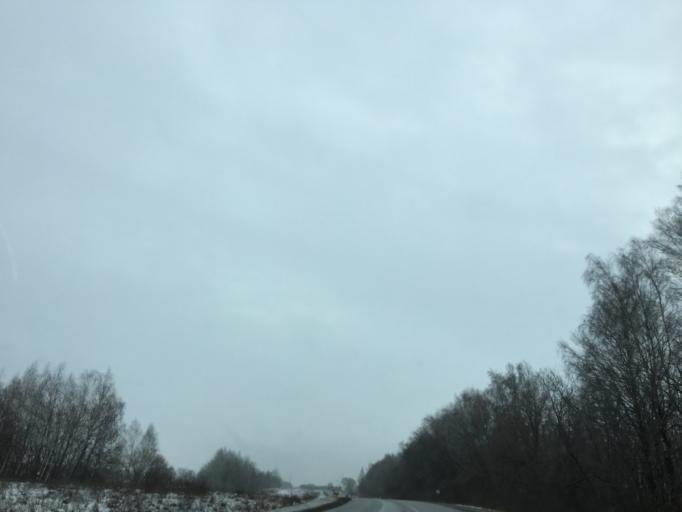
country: RU
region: Tula
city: Borodinskiy
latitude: 54.0320
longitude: 37.8805
